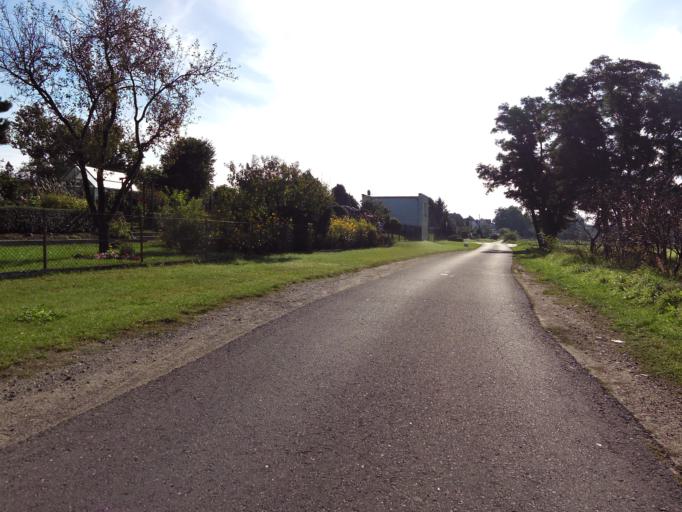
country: DE
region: Saxony-Anhalt
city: Coswig
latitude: 51.8757
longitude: 12.4692
